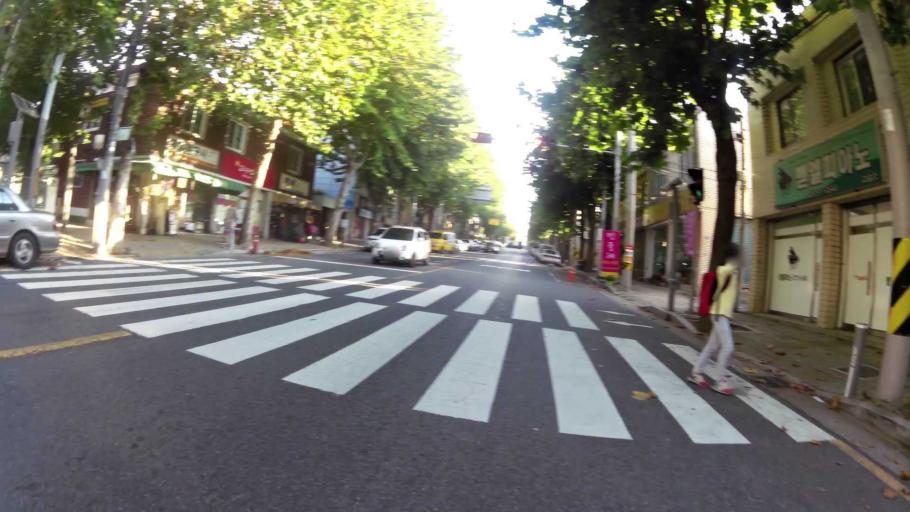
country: KR
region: Daegu
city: Daegu
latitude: 35.8647
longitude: 128.6394
